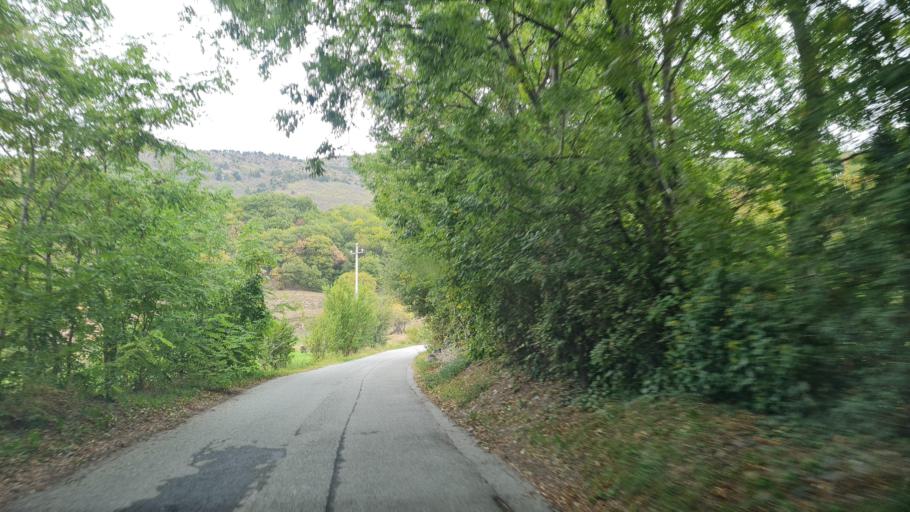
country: IT
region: Aosta Valley
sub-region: Valle d'Aosta
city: Quart
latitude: 45.7430
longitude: 7.4071
